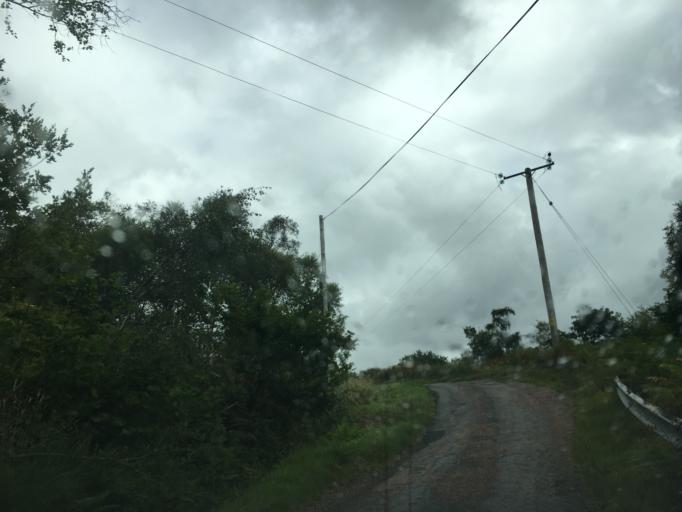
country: GB
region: Scotland
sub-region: Argyll and Bute
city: Oban
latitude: 56.2734
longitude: -5.3667
